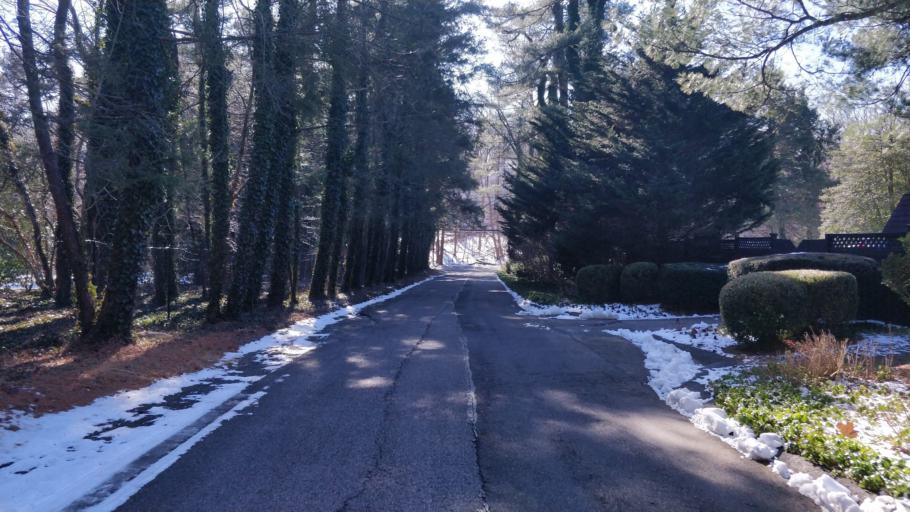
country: US
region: New York
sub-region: Nassau County
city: Old Brookville
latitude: 40.8367
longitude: -73.6107
